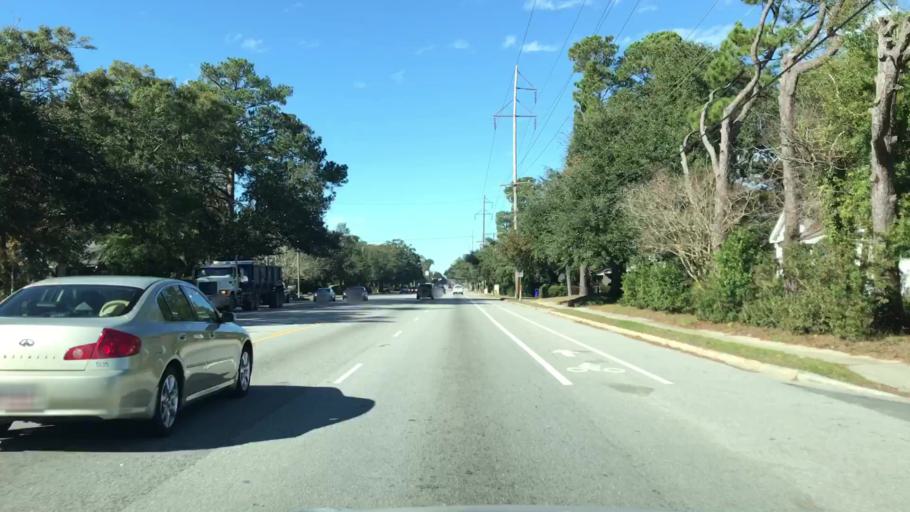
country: US
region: South Carolina
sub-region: Charleston County
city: Charleston
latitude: 32.7826
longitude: -79.9749
